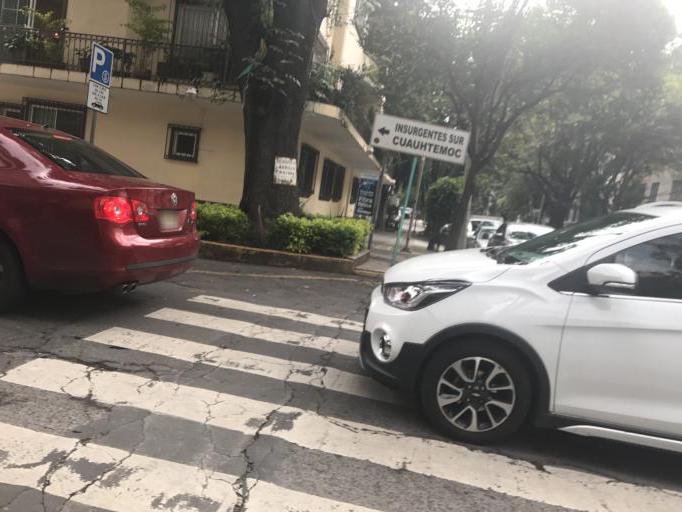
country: MX
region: Mexico City
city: Benito Juarez
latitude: 19.4044
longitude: -99.1703
